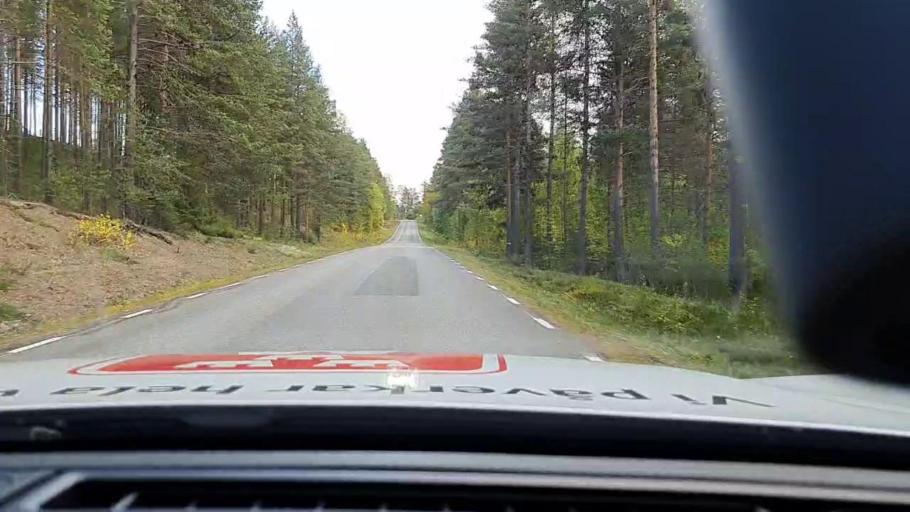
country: SE
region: Vaesterbotten
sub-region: Skelleftea Kommun
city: Langsele
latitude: 64.9426
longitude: 19.9622
